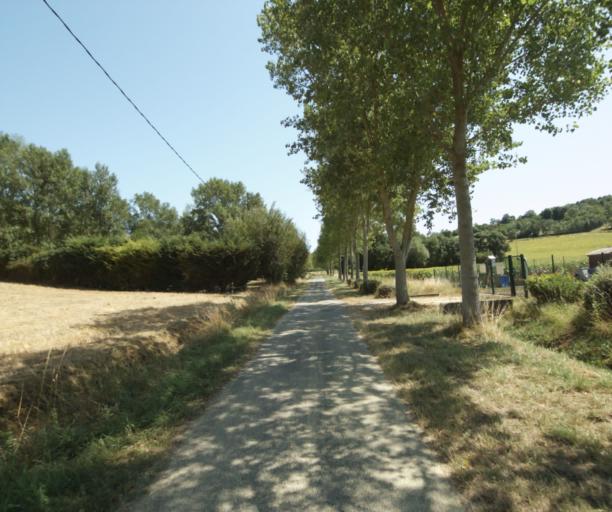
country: FR
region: Midi-Pyrenees
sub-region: Departement de la Haute-Garonne
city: Saint-Felix-Lauragais
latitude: 43.4565
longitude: 1.8795
